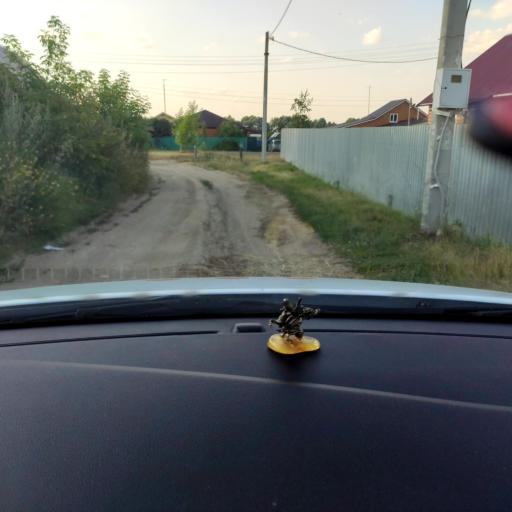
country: RU
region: Tatarstan
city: Pestretsy
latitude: 55.6152
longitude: 49.4960
